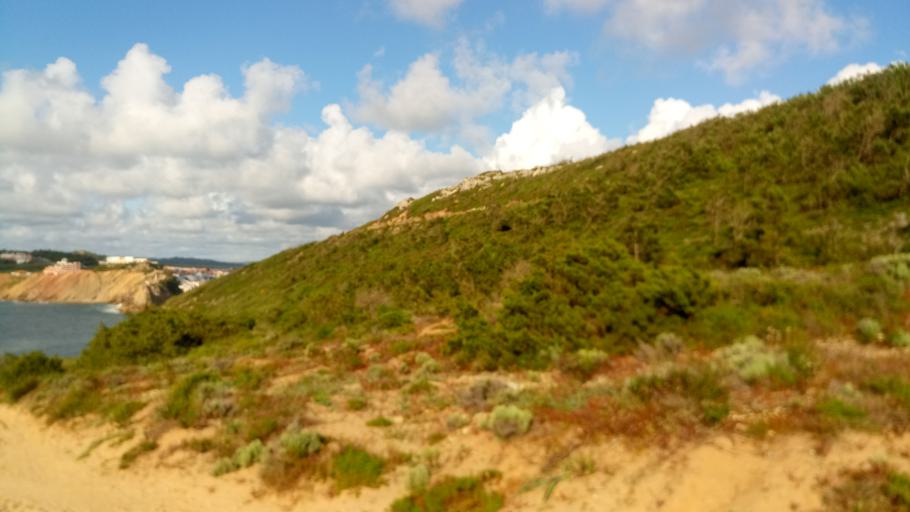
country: PT
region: Leiria
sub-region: Caldas da Rainha
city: Caldas da Rainha
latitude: 39.5064
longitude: -9.1504
